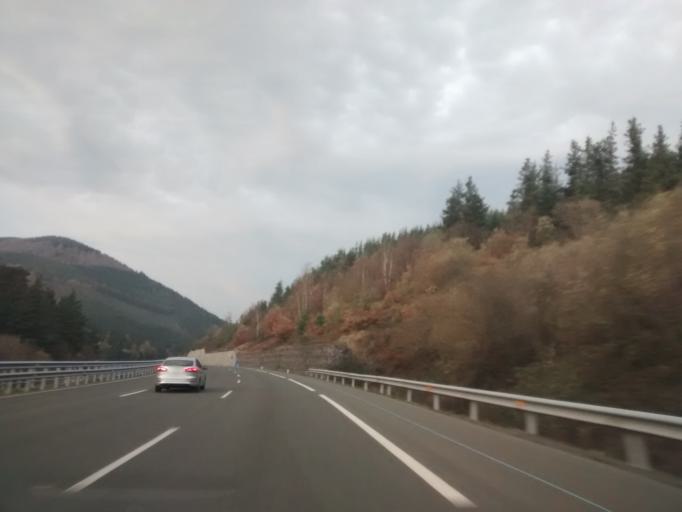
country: ES
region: Basque Country
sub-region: Bizkaia
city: Elexalde
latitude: 43.0850
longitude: -2.9144
